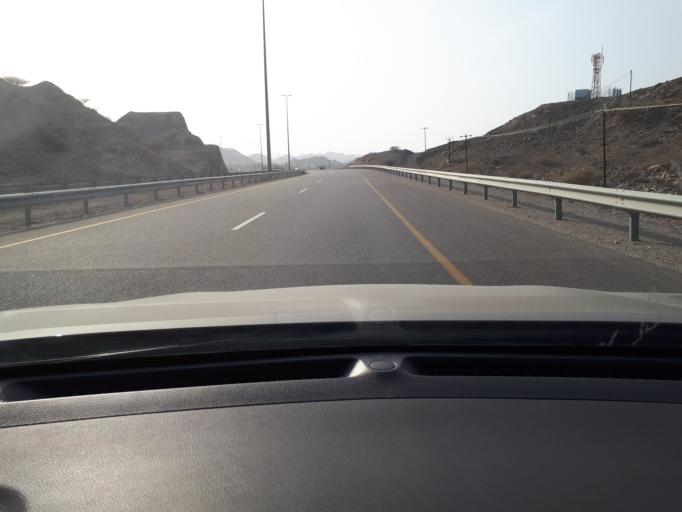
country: OM
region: Muhafazat Masqat
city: Muscat
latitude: 23.2620
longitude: 58.7669
